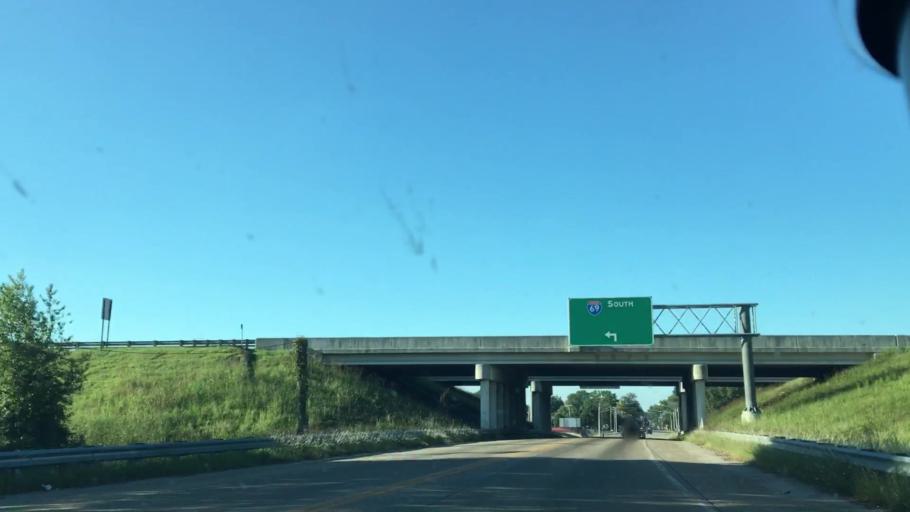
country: US
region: Indiana
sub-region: Vanderburgh County
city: Evansville
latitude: 37.9386
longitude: -87.4928
